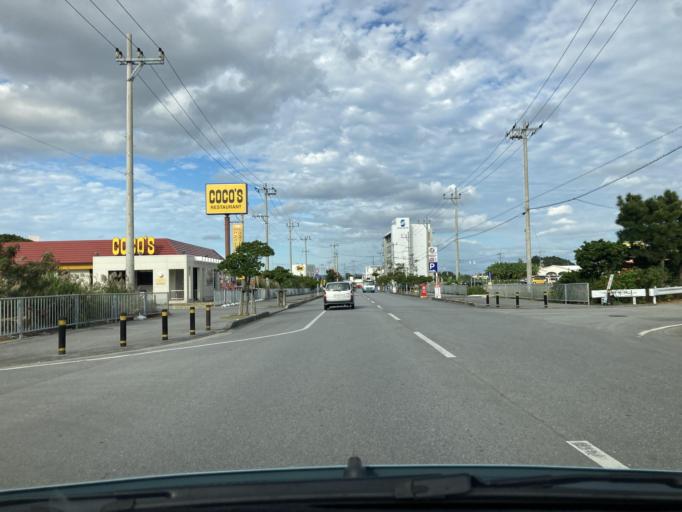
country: JP
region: Okinawa
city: Okinawa
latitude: 26.3679
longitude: 127.8252
